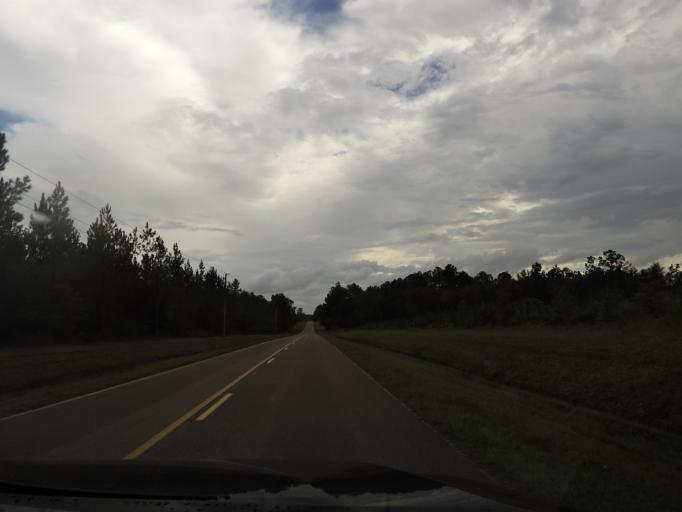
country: US
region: Florida
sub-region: Duval County
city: Baldwin
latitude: 30.4843
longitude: -81.9989
